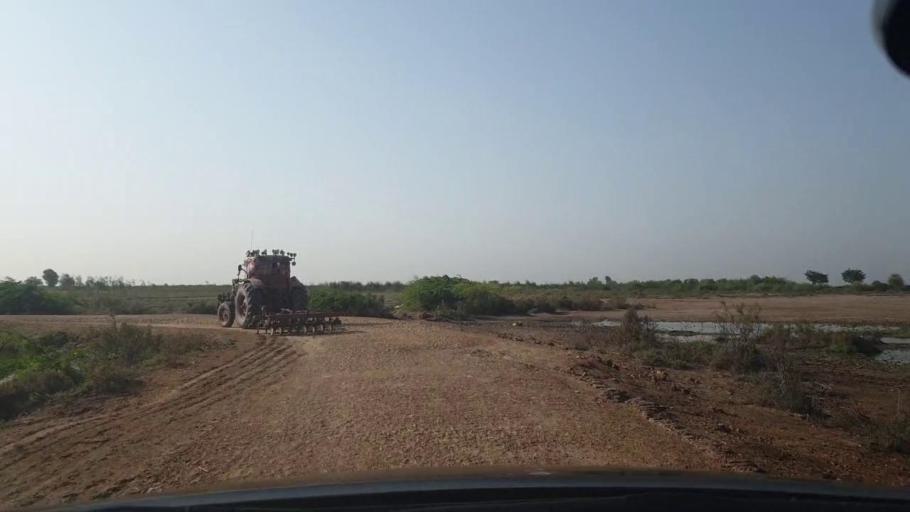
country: PK
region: Sindh
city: Tando Bago
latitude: 24.6507
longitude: 69.1368
